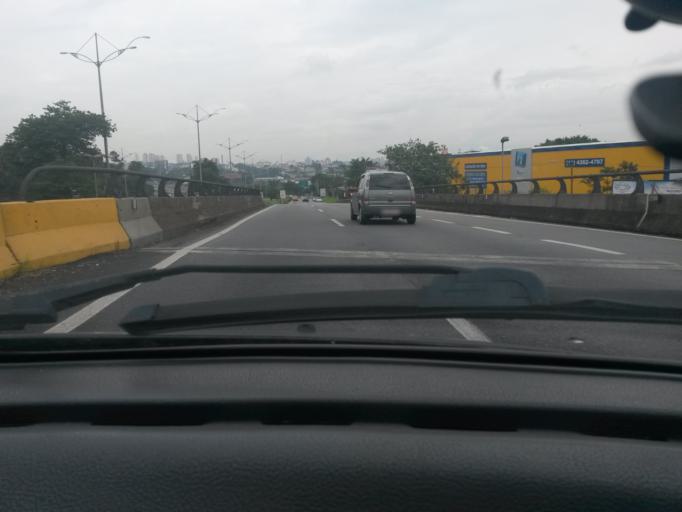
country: BR
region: Sao Paulo
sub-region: Sao Caetano Do Sul
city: Sao Caetano do Sul
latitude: -23.6485
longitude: -46.5815
